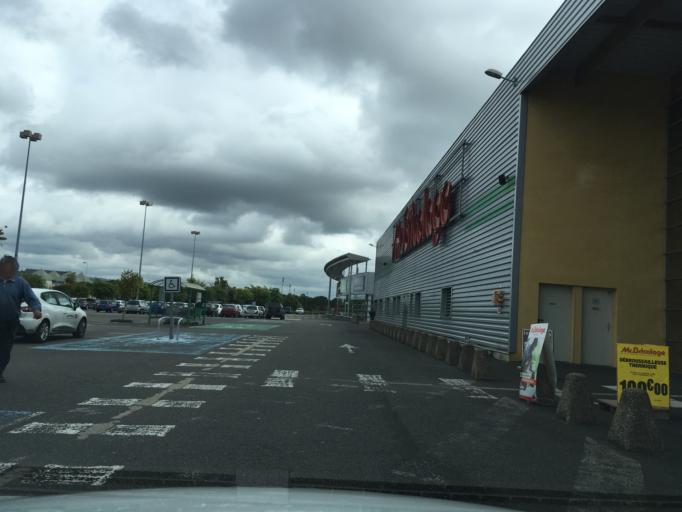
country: FR
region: Limousin
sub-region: Departement de la Correze
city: Saint-Pantaleon-de-Larche
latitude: 45.1429
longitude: 1.4724
